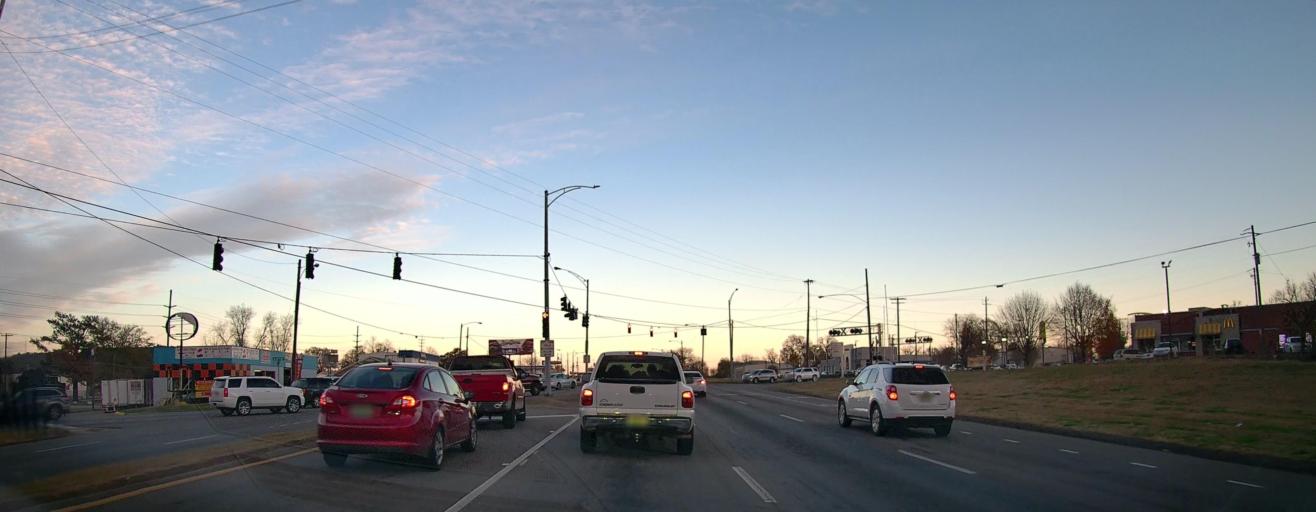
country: US
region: Alabama
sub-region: Etowah County
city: Gadsden
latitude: 34.0212
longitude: -86.0205
